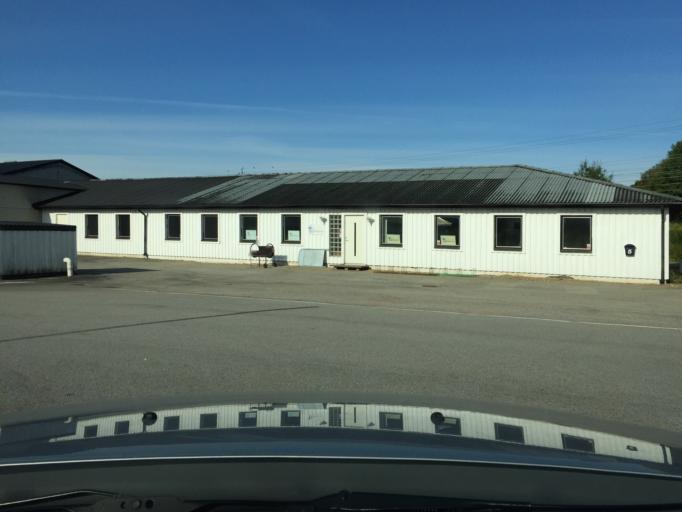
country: SE
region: Skane
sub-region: Hoors Kommun
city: Hoeoer
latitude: 55.9484
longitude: 13.5579
